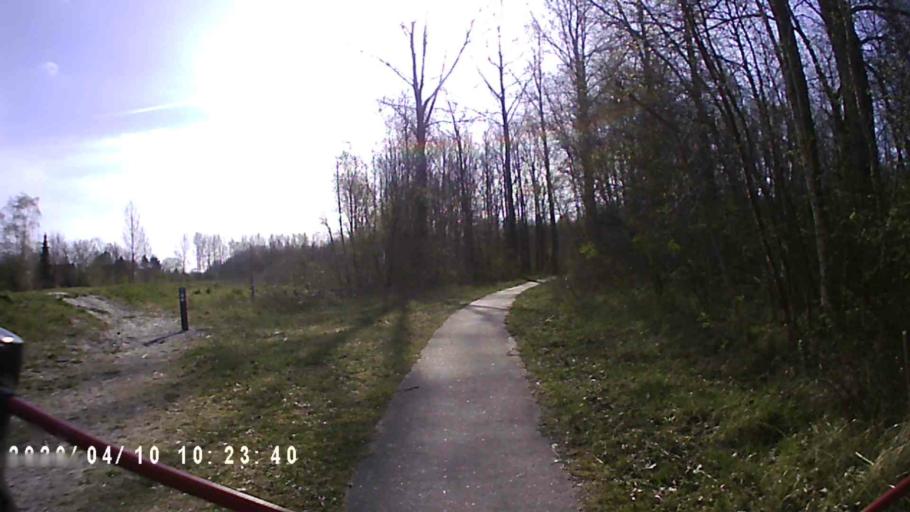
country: NL
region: Friesland
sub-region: Gemeente Dongeradeel
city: Anjum
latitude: 53.3853
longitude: 6.2167
